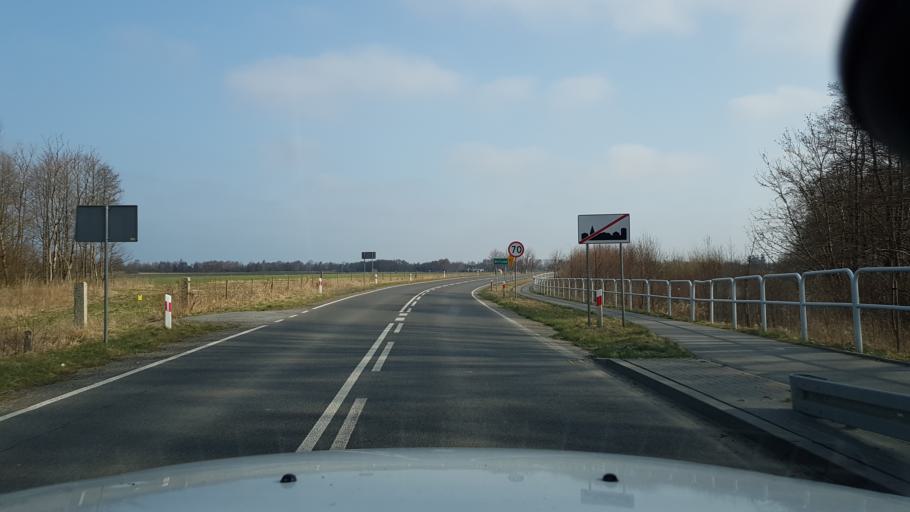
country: PL
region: West Pomeranian Voivodeship
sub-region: Powiat koszalinski
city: Sianow
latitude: 54.3169
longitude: 16.3024
